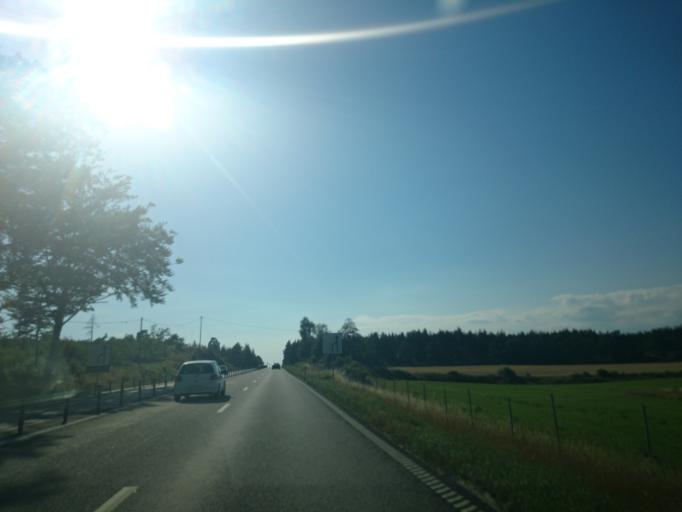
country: SE
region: Blekinge
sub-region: Karlskrona Kommun
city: Nattraby
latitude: 56.1986
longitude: 15.4201
